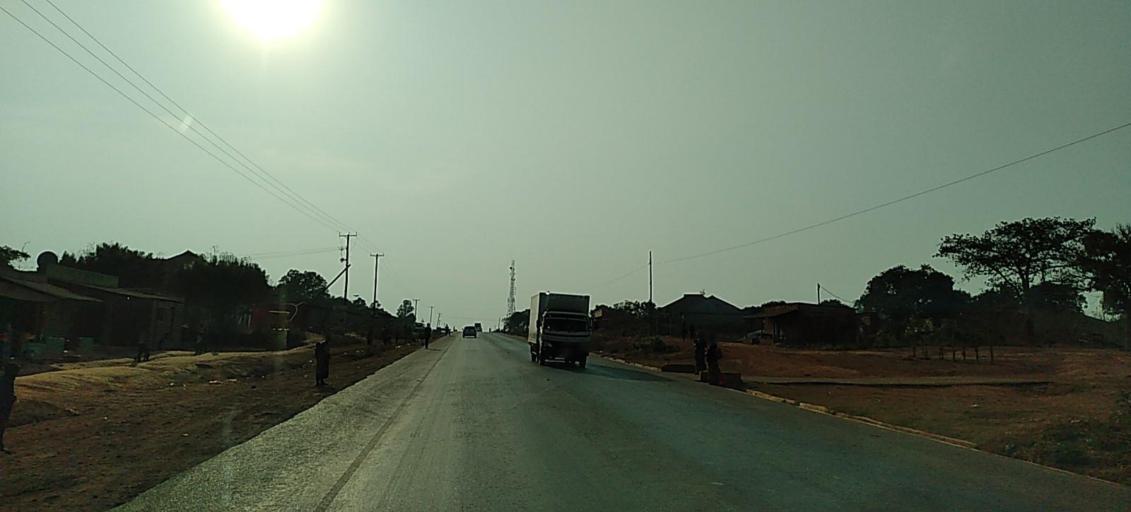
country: ZM
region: North-Western
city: Solwezi
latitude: -12.1910
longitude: 26.4394
